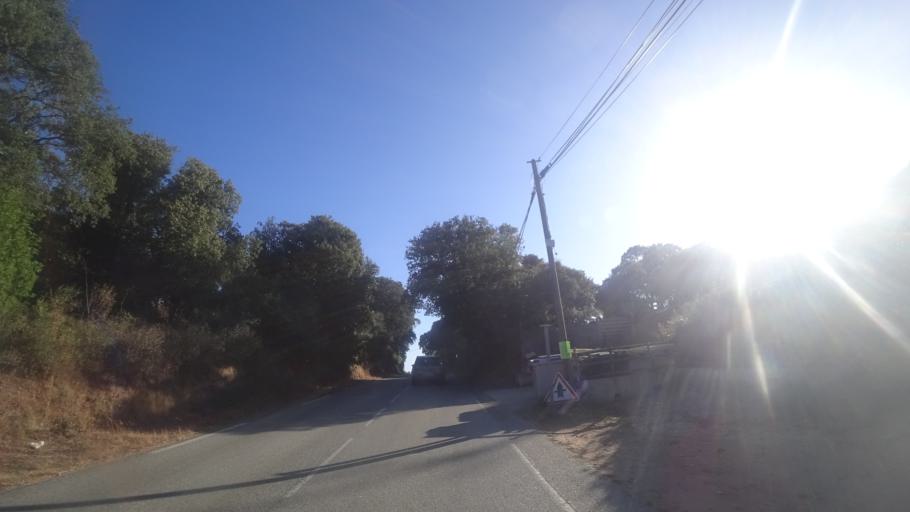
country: FR
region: Corsica
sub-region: Departement de la Corse-du-Sud
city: Cargese
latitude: 42.1623
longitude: 8.5980
